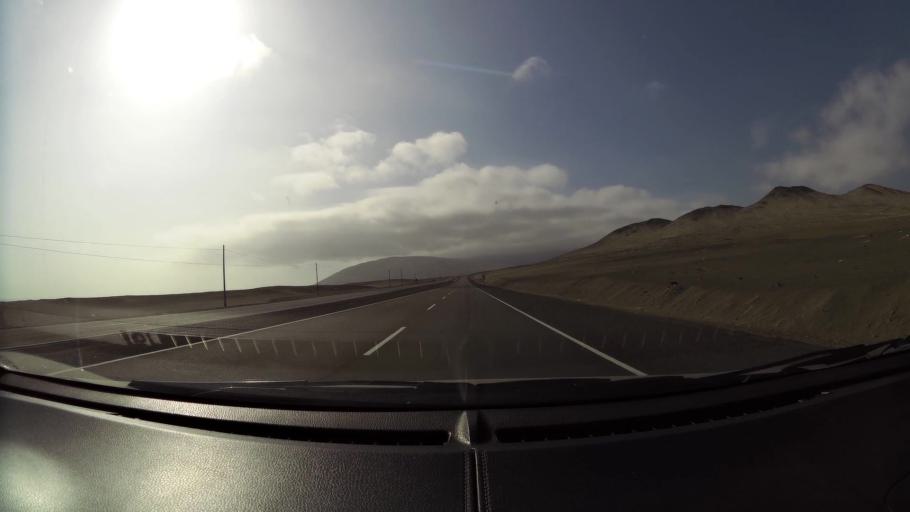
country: PE
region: Ancash
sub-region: Provincia de Casma
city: Casma
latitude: -9.6983
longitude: -78.2799
